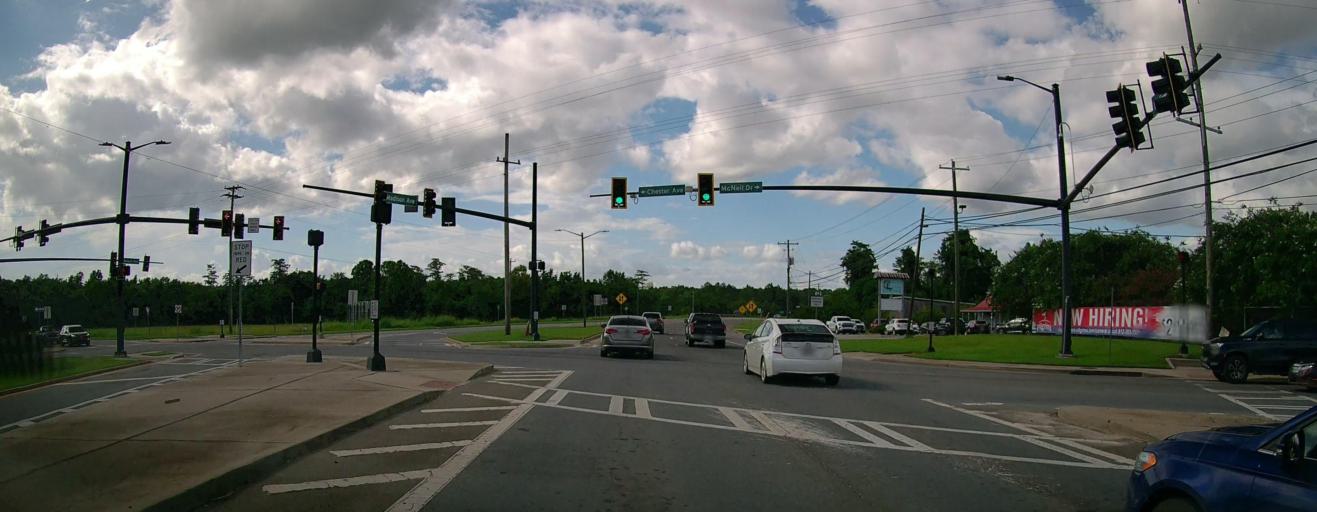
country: US
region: Georgia
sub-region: Coffee County
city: Douglas
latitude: 31.5260
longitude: -82.8502
